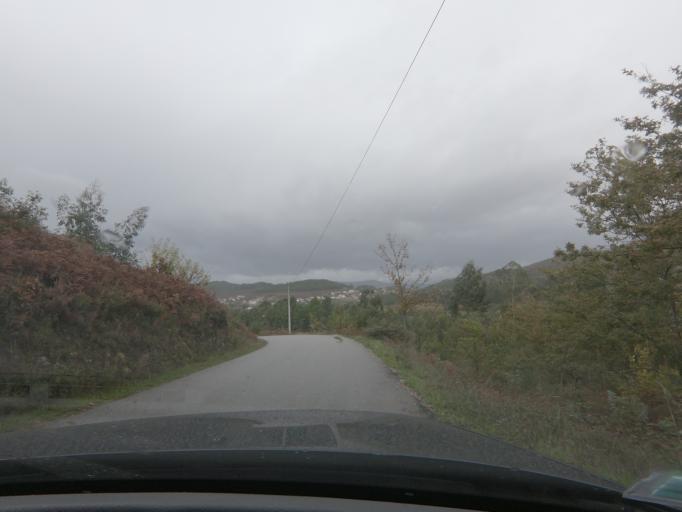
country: PT
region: Vila Real
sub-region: Mondim de Basto
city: Mondim de Basto
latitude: 41.3720
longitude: -7.9417
